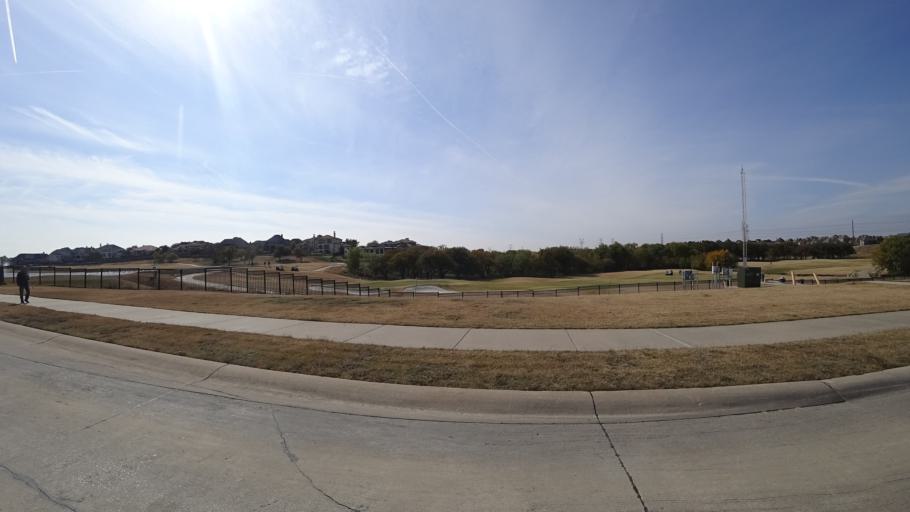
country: US
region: Texas
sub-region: Denton County
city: The Colony
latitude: 33.0392
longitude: -96.9007
